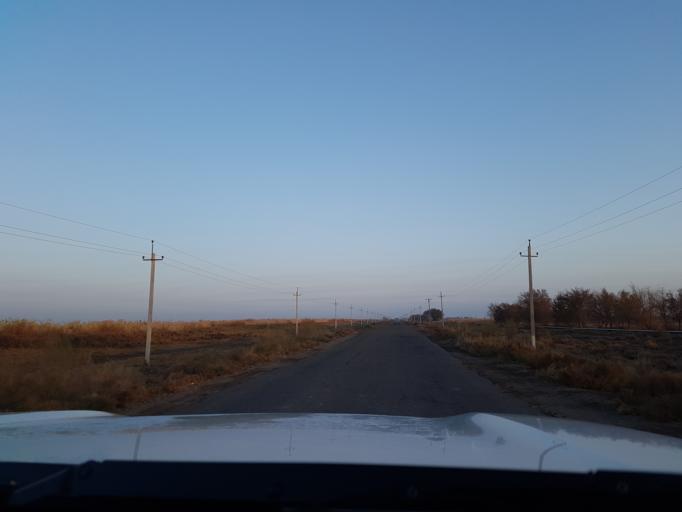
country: TM
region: Dasoguz
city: Koeneuergench
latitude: 41.8303
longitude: 58.7040
